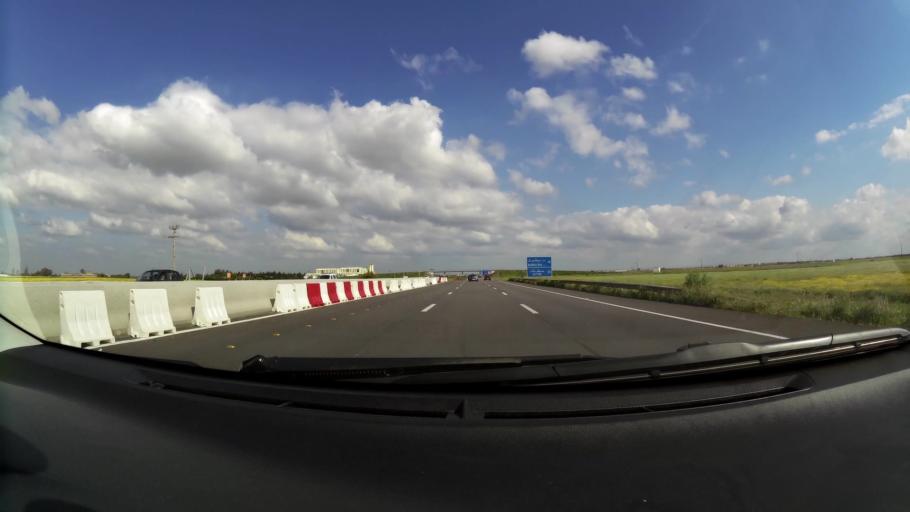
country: MA
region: Chaouia-Ouardigha
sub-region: Settat Province
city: Berrechid
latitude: 33.3144
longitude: -7.5984
